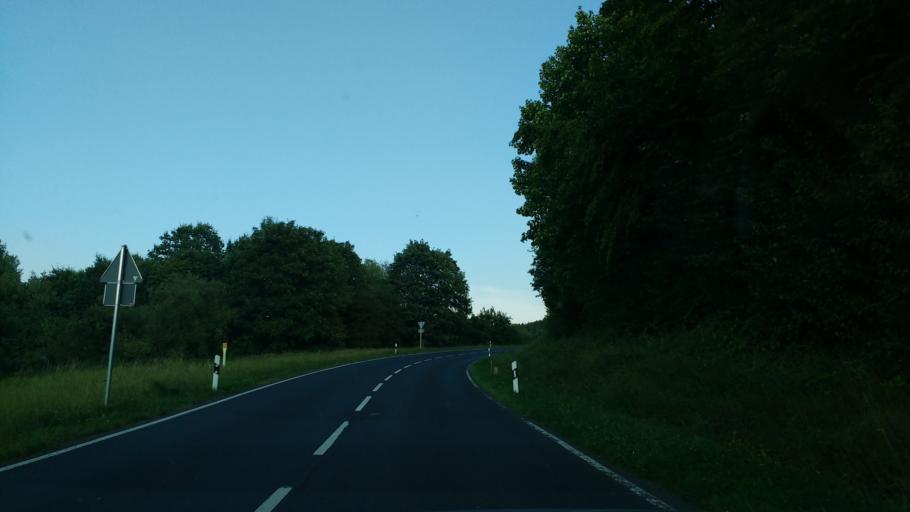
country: DE
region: Bavaria
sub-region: Regierungsbezirk Unterfranken
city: Oberthulba
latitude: 50.1961
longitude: 9.9638
